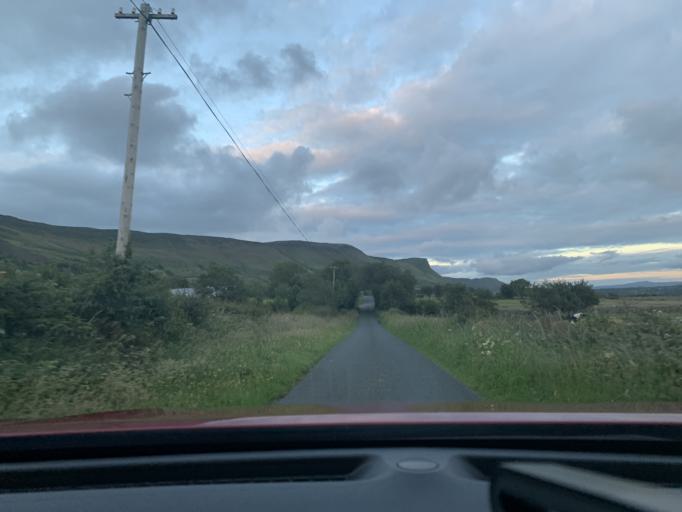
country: IE
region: Connaught
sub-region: Sligo
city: Sligo
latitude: 54.3571
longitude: -8.5013
